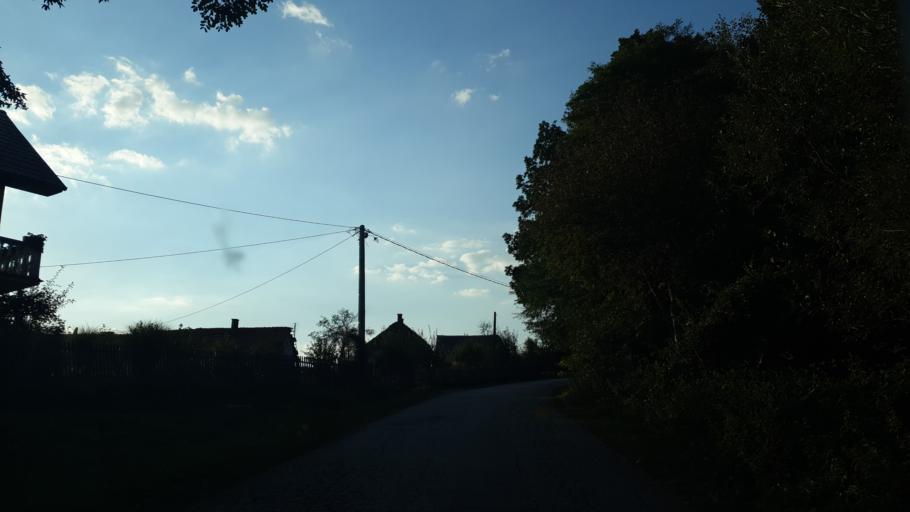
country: RS
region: Central Serbia
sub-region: Zlatiborski Okrug
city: Kosjeric
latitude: 43.9908
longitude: 20.0057
